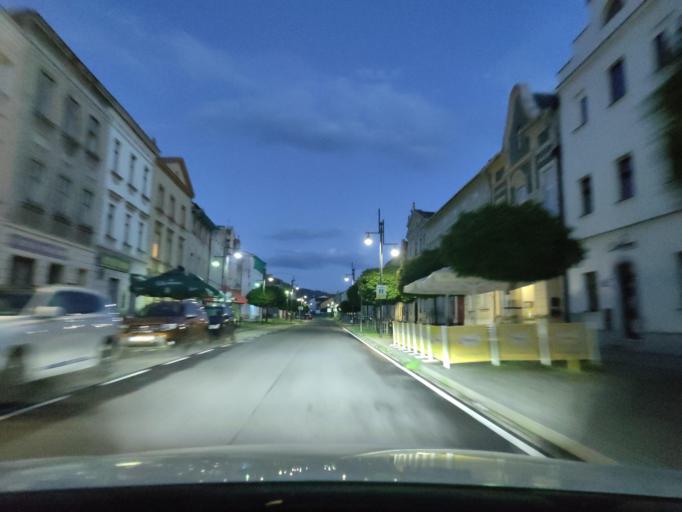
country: CZ
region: Olomoucky
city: Zlate Hory
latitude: 50.2635
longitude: 17.3962
